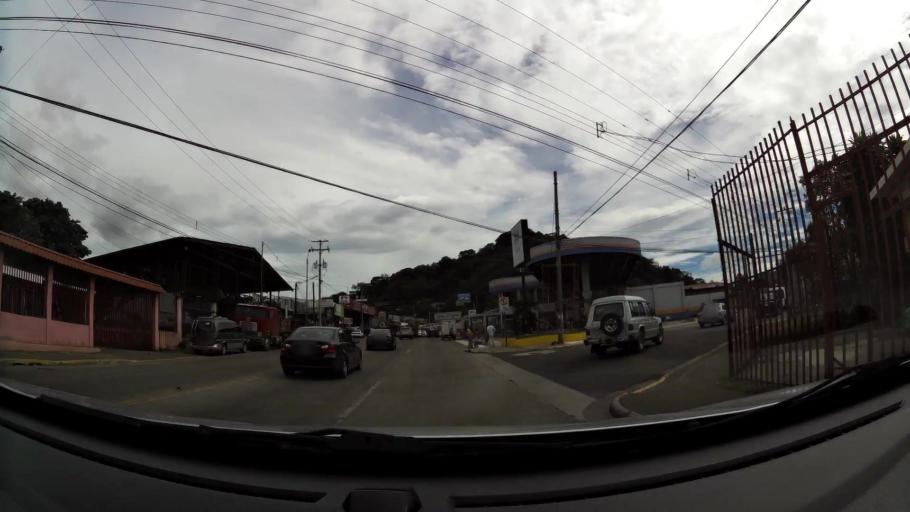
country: CR
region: San Jose
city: Curridabat
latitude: 9.9039
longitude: -84.0463
